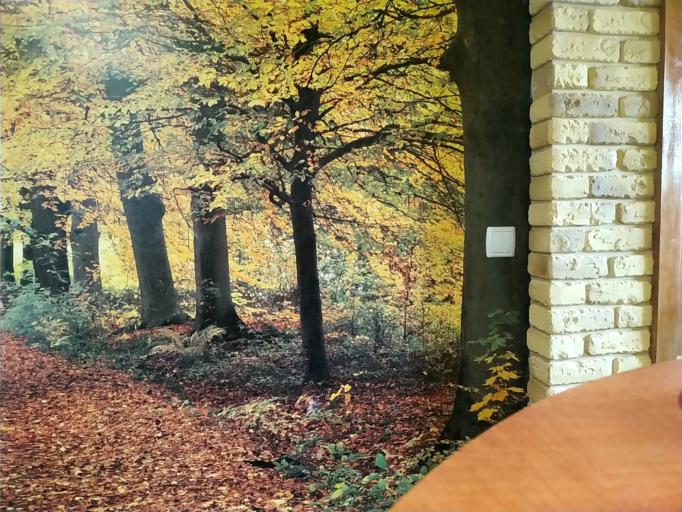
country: RU
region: Novgorod
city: Opechenskiy Posad
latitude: 58.2679
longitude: 34.0223
